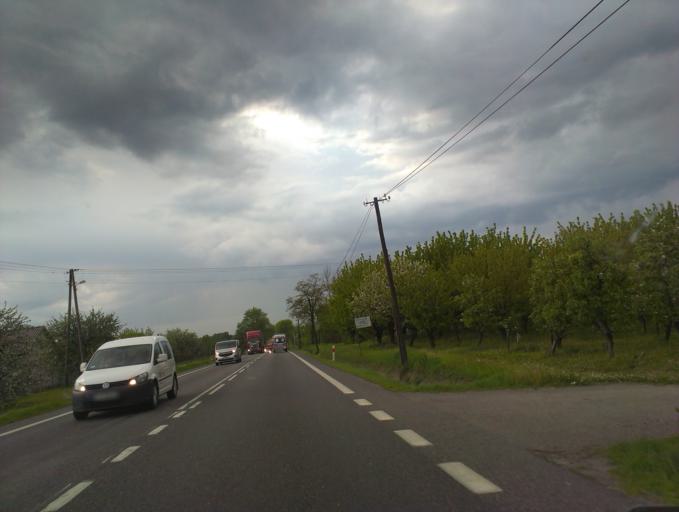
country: PL
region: Masovian Voivodeship
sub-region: Powiat grojecki
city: Pniewy
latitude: 51.9188
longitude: 20.6786
